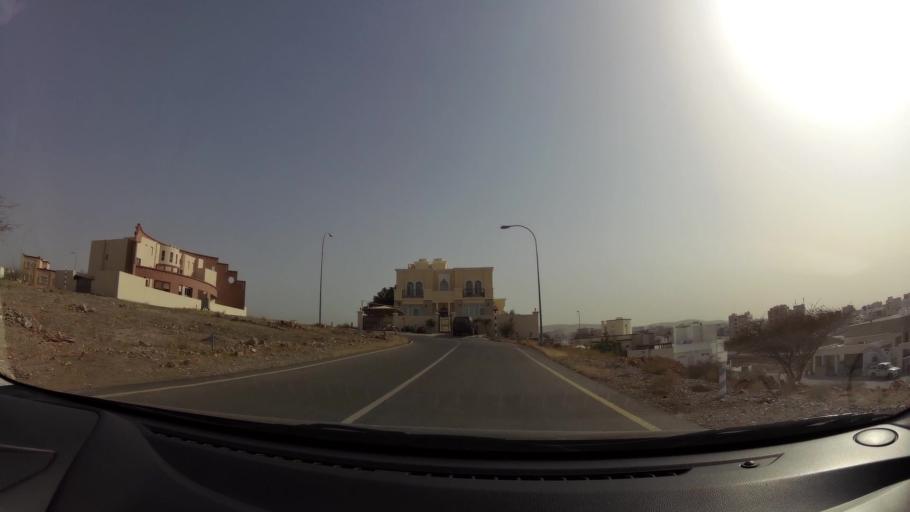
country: OM
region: Muhafazat Masqat
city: Bawshar
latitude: 23.5578
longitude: 58.3533
